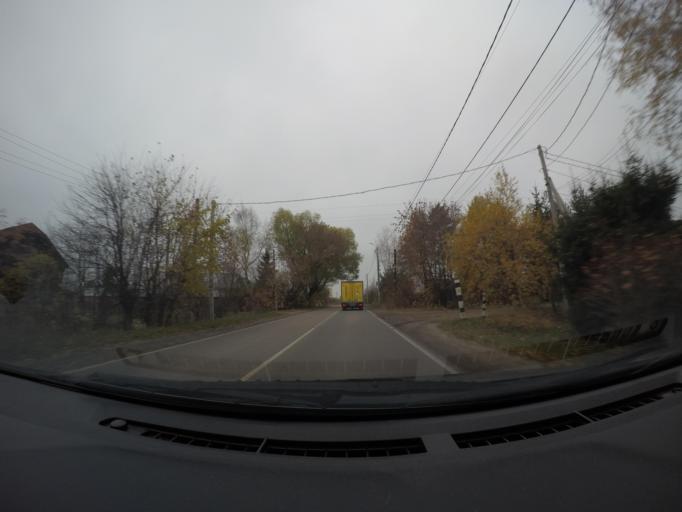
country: RU
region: Moskovskaya
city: Gzhel'
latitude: 55.5775
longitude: 38.3960
